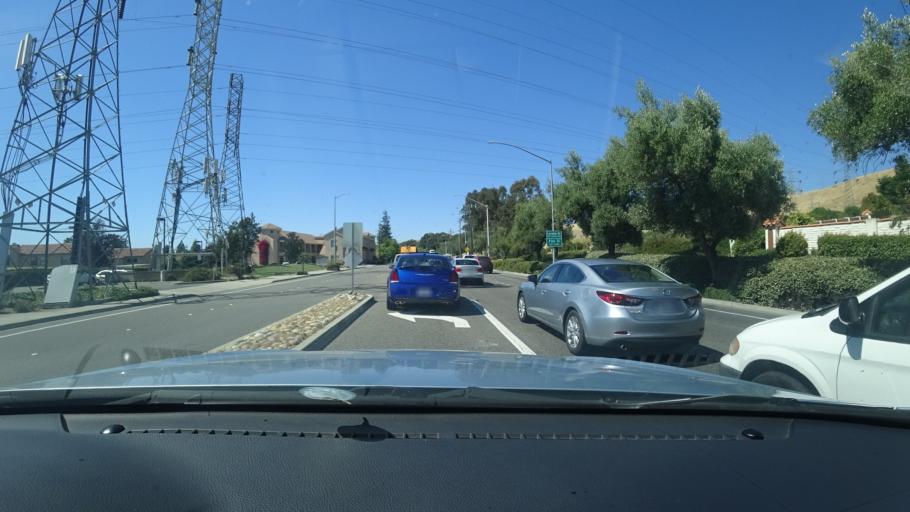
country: US
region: California
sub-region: Alameda County
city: Fremont
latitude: 37.5240
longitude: -121.9178
